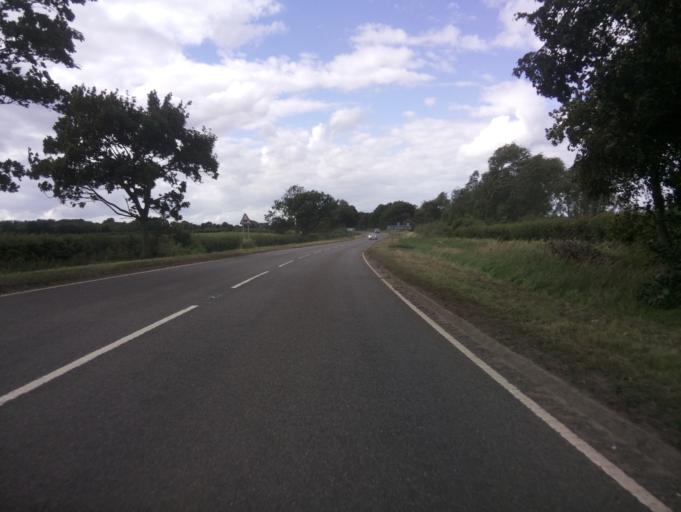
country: GB
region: England
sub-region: Leicestershire
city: Market Bosworth
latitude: 52.6232
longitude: -1.4821
